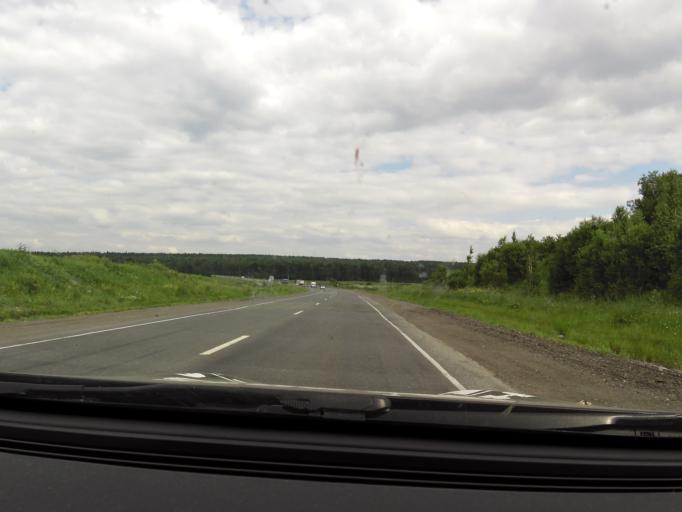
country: RU
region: Sverdlovsk
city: Druzhinino
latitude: 56.8095
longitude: 59.5407
